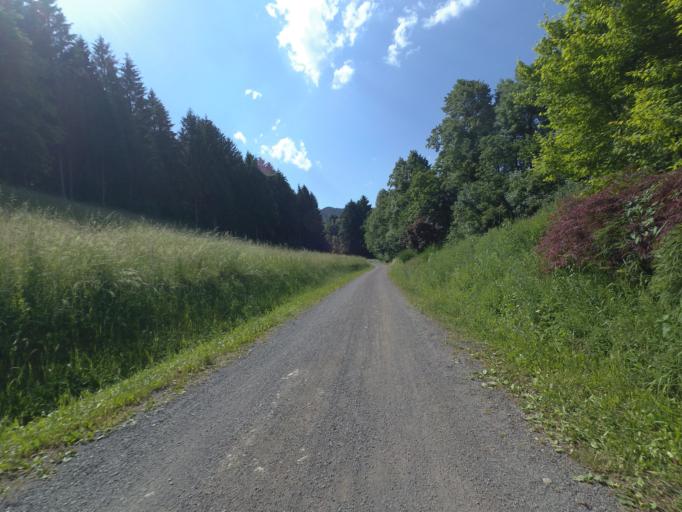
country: AT
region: Carinthia
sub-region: Politischer Bezirk Spittal an der Drau
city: Millstatt
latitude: 46.7732
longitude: 13.6038
